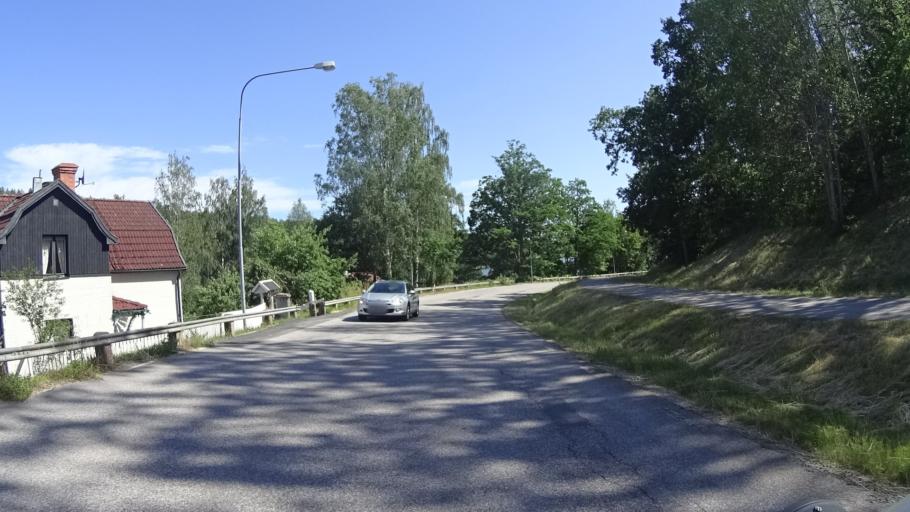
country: SE
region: Kalmar
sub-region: Vasterviks Kommun
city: Gamleby
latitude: 57.9042
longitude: 16.4134
